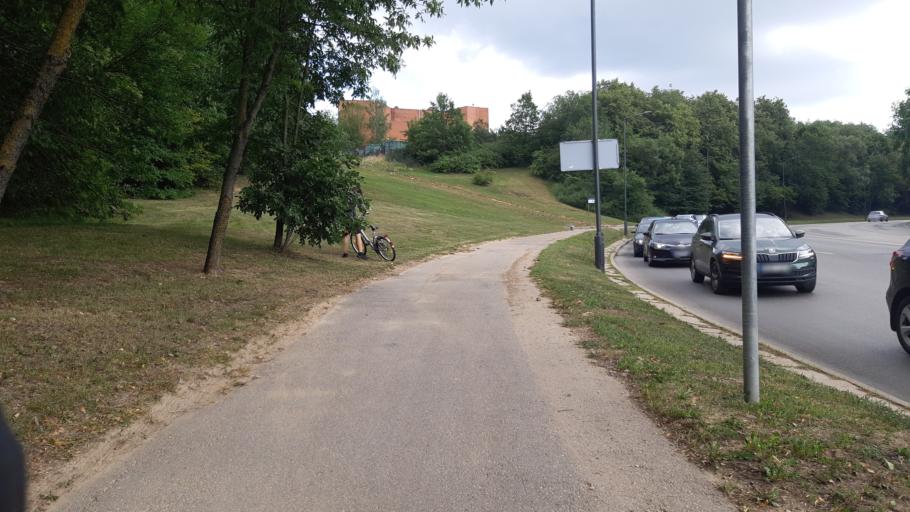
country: LT
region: Kauno apskritis
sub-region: Kaunas
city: Eiguliai
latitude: 54.9306
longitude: 23.9183
